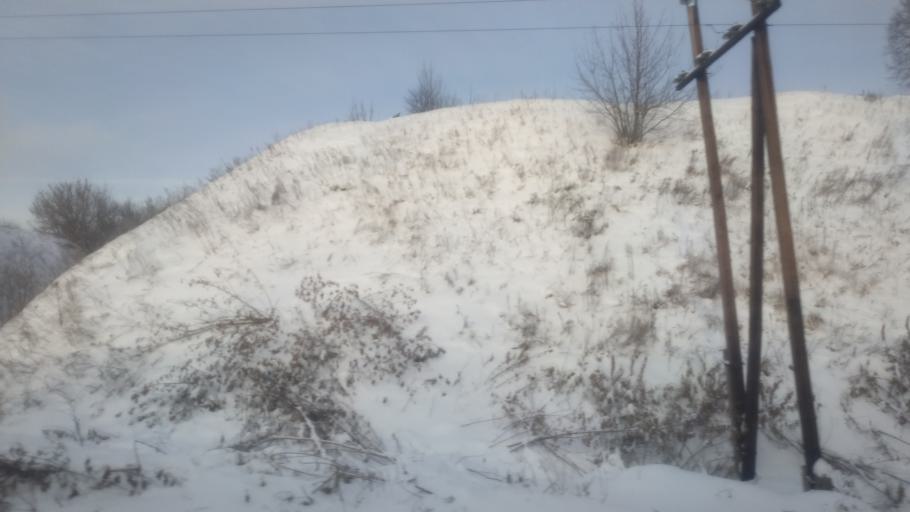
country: RU
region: Kirov
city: Sosnovka
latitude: 56.2536
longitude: 51.2517
